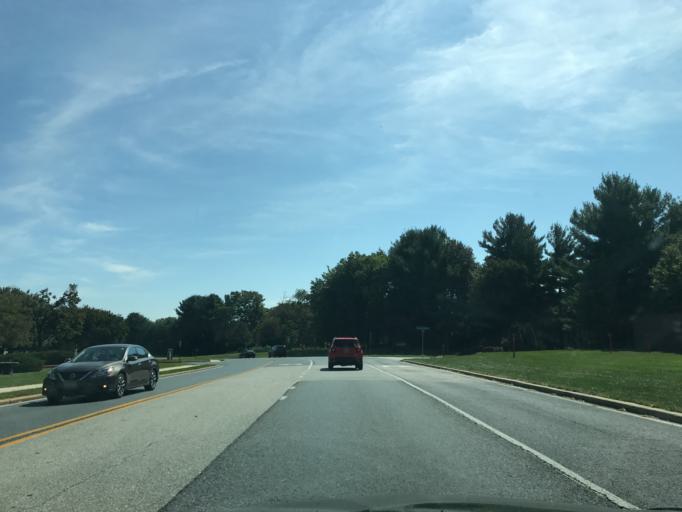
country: US
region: Maryland
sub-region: Howard County
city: Columbia
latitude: 39.2286
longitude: -76.8272
